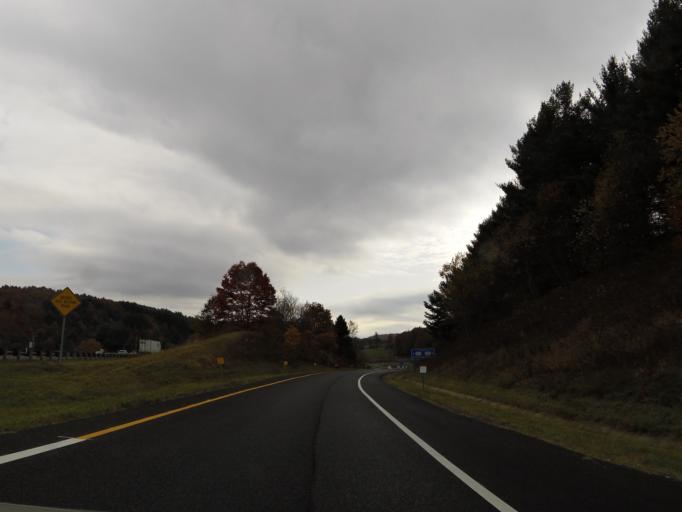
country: US
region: Virginia
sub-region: Carroll County
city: Hillsville
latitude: 36.6764
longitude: -80.7111
